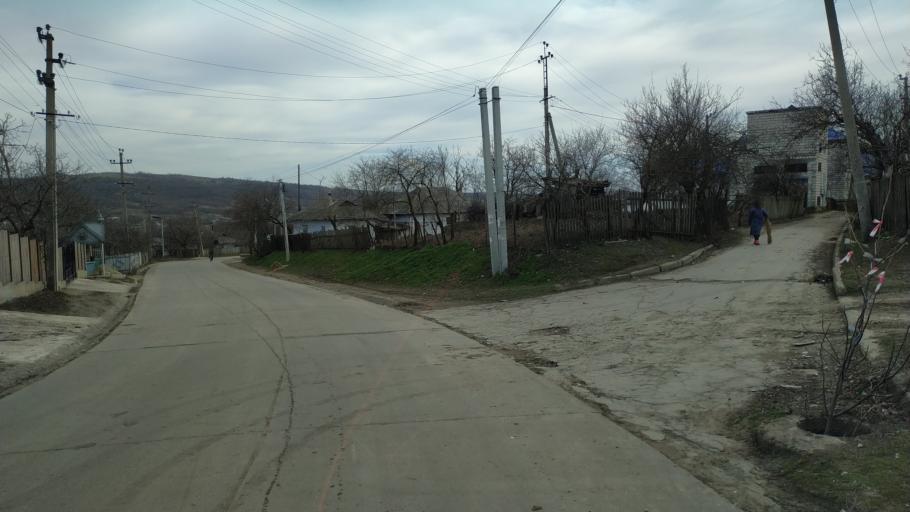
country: MD
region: Nisporeni
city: Nisporeni
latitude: 46.9264
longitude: 28.2622
